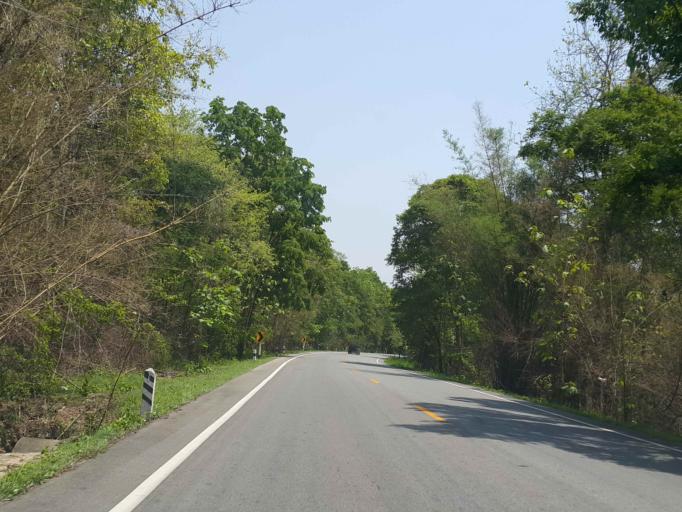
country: TH
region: Chiang Mai
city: Mae Taeng
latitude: 19.0798
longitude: 98.9794
